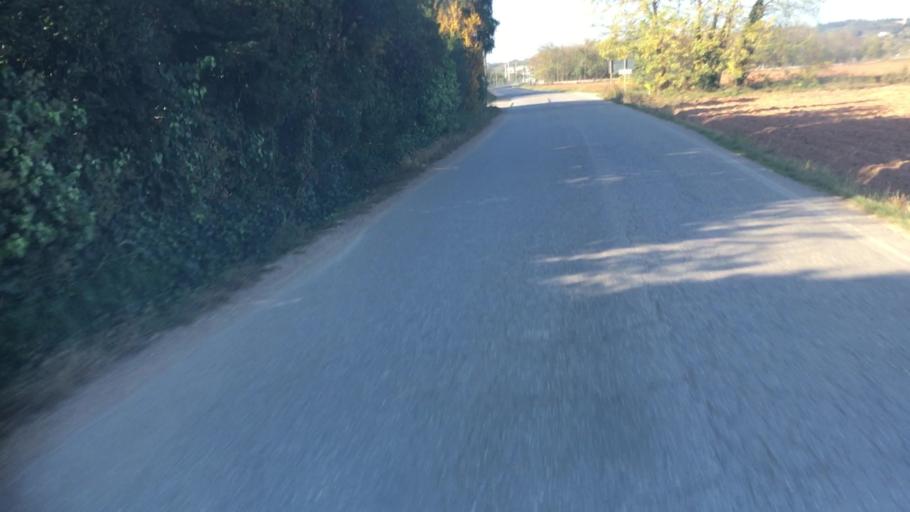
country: IT
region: Lombardy
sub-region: Provincia di Mantova
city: Guidizzolo
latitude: 45.3226
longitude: 10.6005
